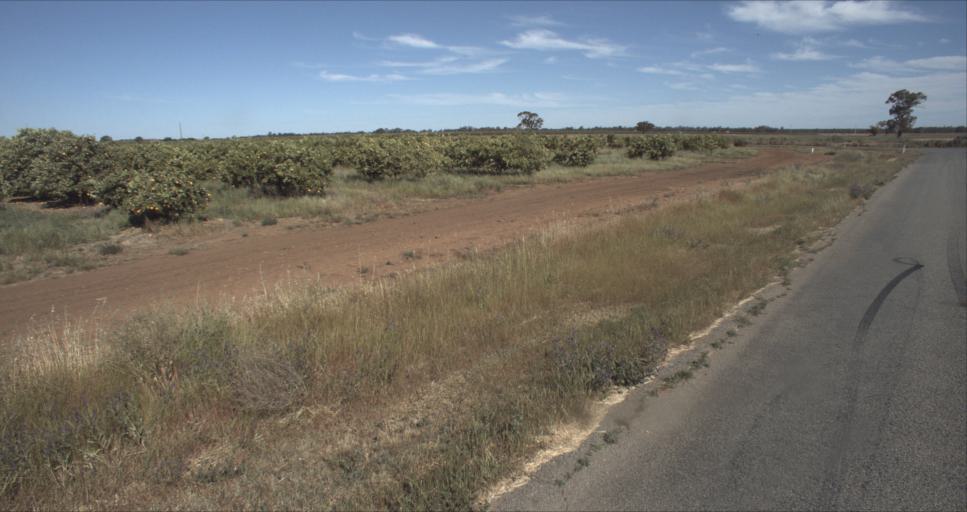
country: AU
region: New South Wales
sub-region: Leeton
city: Leeton
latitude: -34.5870
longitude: 146.3787
